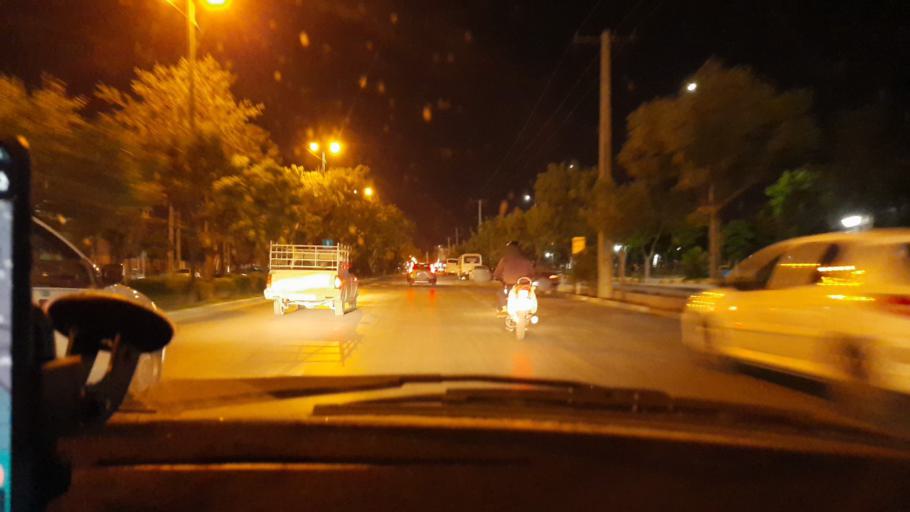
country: IR
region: Markazi
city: Arak
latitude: 34.1068
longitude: 49.6968
